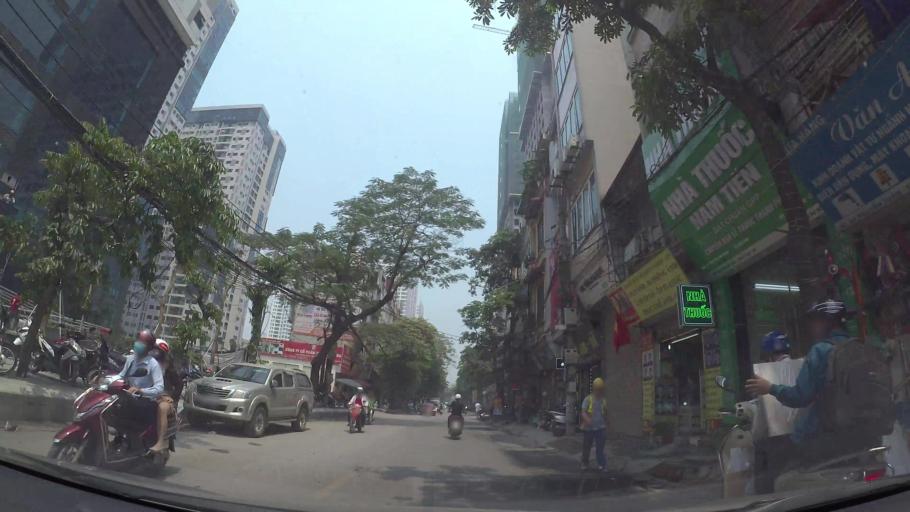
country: VN
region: Ha Noi
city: Thanh Xuan
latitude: 20.9951
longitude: 105.8060
